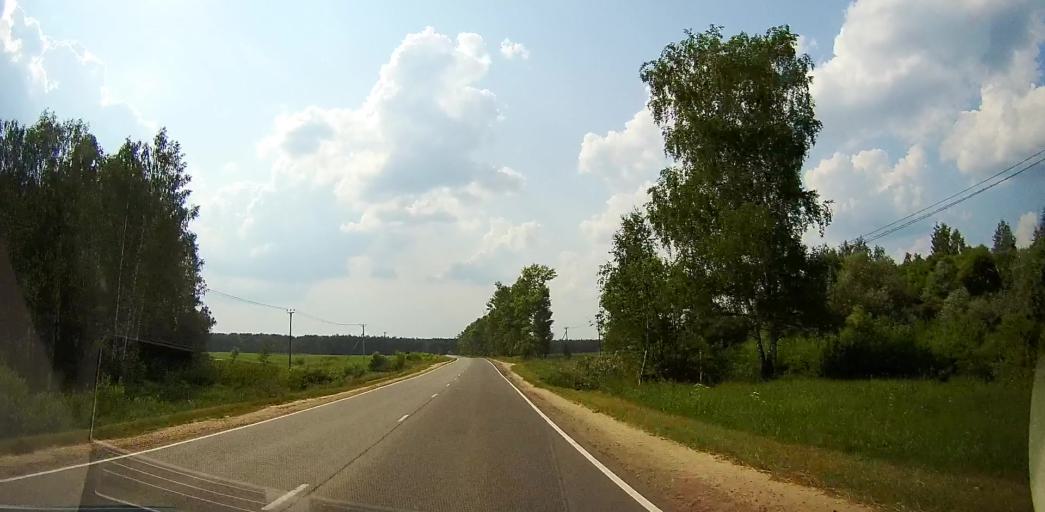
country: RU
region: Moskovskaya
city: Zhilevo
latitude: 55.0569
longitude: 37.9675
